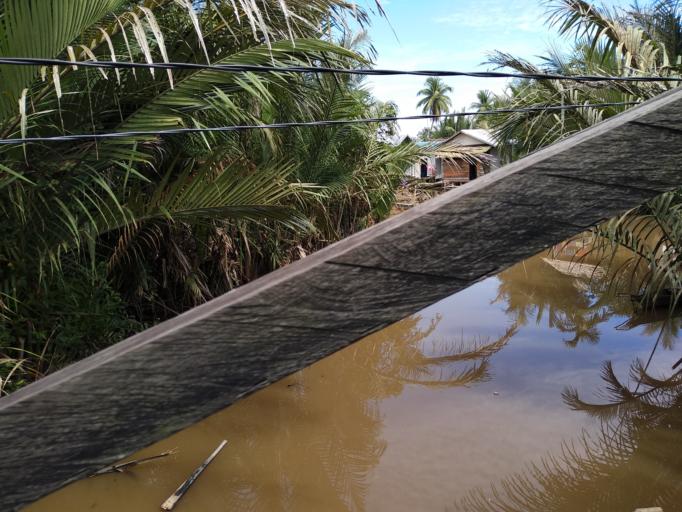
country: ID
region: South Kalimantan
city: Tabunganen
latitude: -3.4135
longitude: 114.4909
